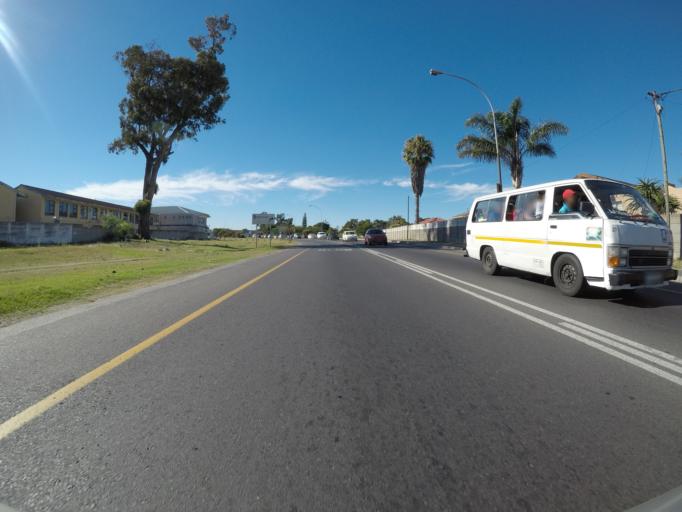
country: ZA
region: Western Cape
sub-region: City of Cape Town
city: Kraaifontein
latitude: -33.9363
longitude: 18.6768
